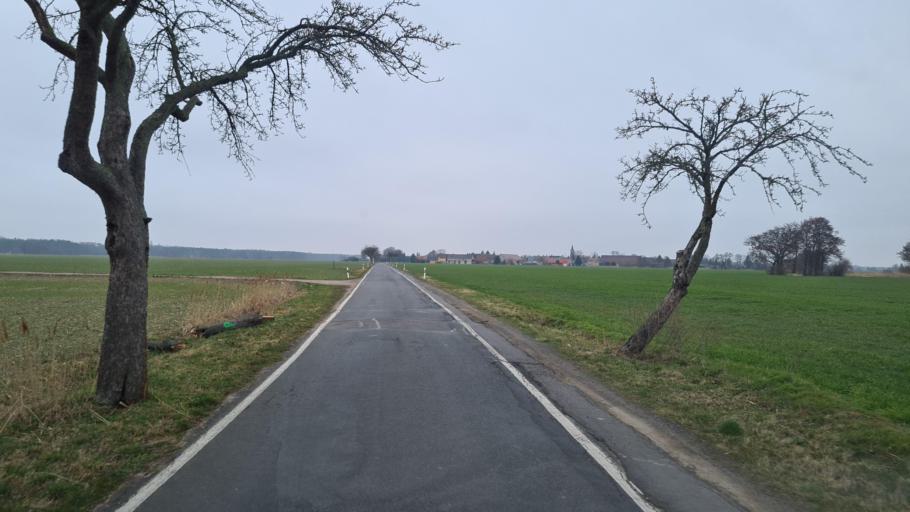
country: DE
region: Brandenburg
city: Herzberg
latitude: 51.6560
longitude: 13.1824
